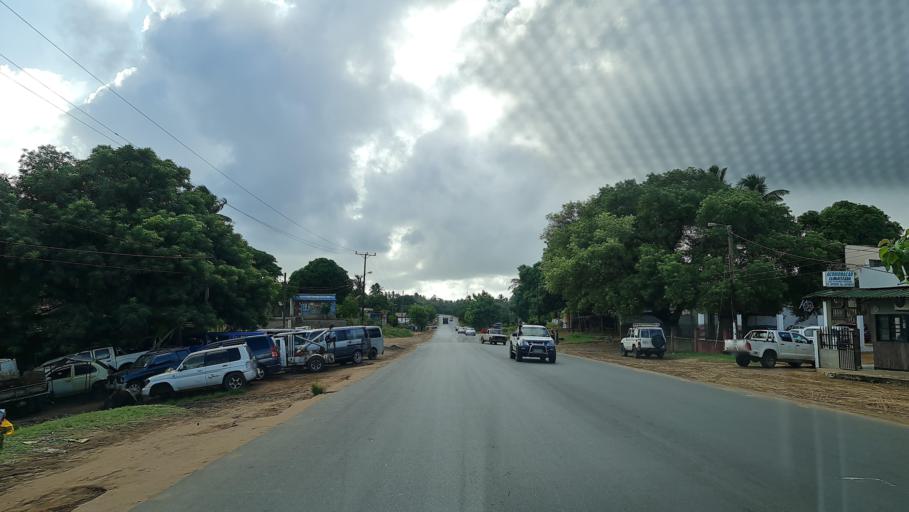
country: MZ
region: Gaza
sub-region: Xai-Xai District
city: Xai-Xai
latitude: -25.0564
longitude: 33.6735
